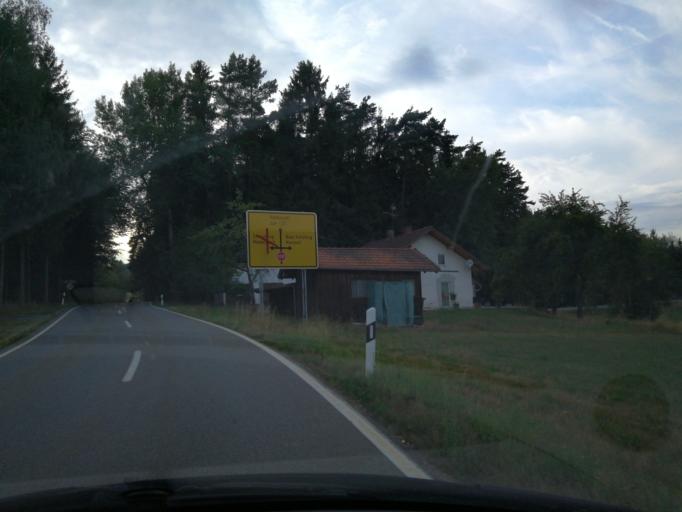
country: DE
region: Bavaria
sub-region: Lower Bavaria
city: Haibach
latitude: 49.0308
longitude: 12.7075
